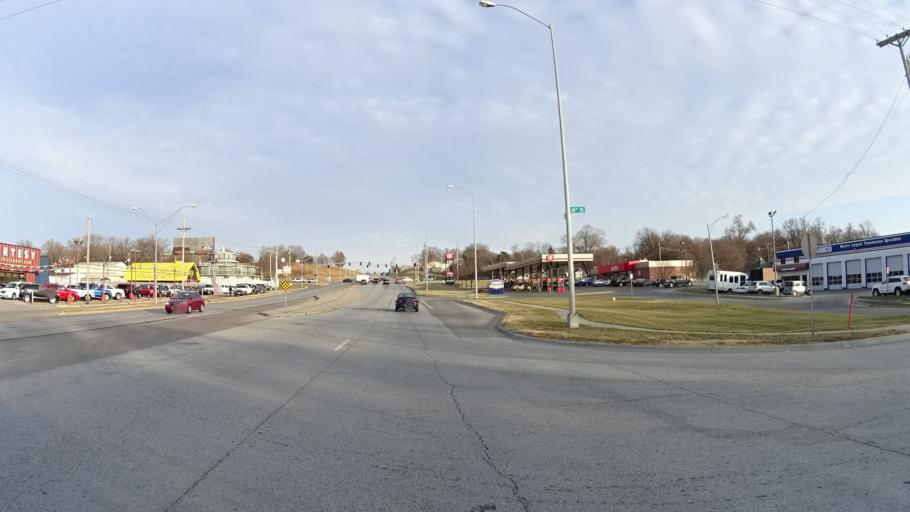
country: US
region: Nebraska
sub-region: Douglas County
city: Ralston
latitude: 41.2124
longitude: -96.0072
